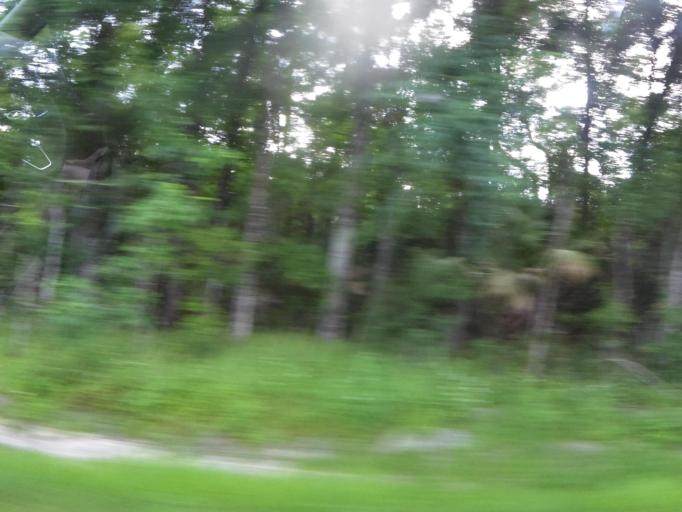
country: US
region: Florida
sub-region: Nassau County
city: Callahan
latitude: 30.5951
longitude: -81.8620
